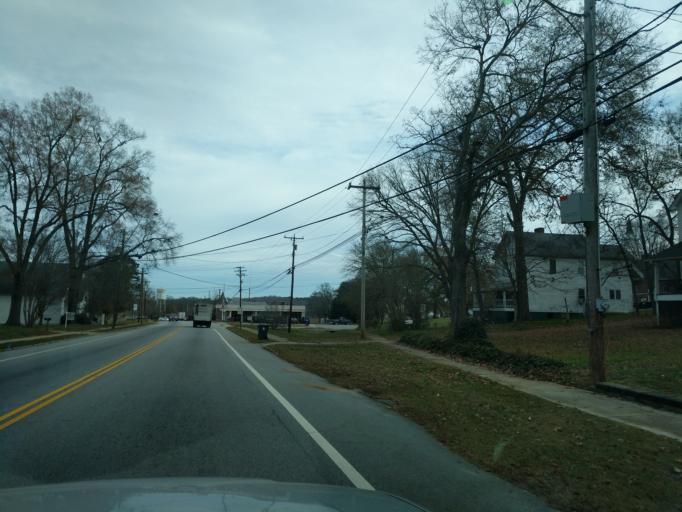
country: US
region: South Carolina
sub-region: Anderson County
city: Williamston
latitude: 34.6426
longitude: -82.4621
